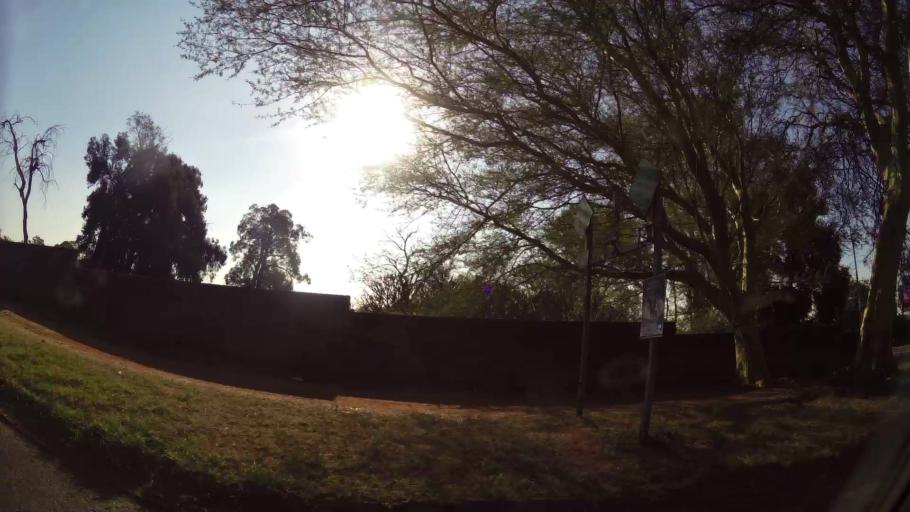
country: ZA
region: North-West
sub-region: Bojanala Platinum District Municipality
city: Rustenburg
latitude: -25.6763
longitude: 27.2462
